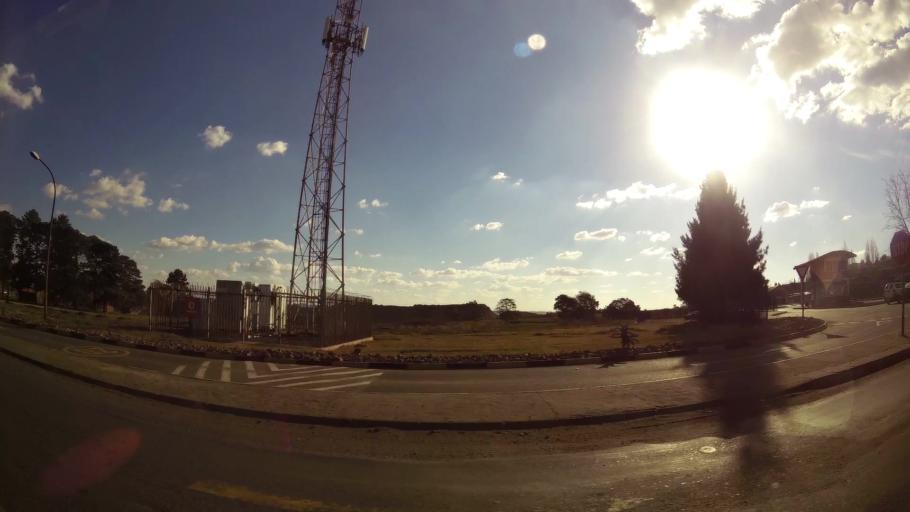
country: ZA
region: Mpumalanga
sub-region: Nkangala District Municipality
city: Witbank
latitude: -25.8712
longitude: 29.1659
